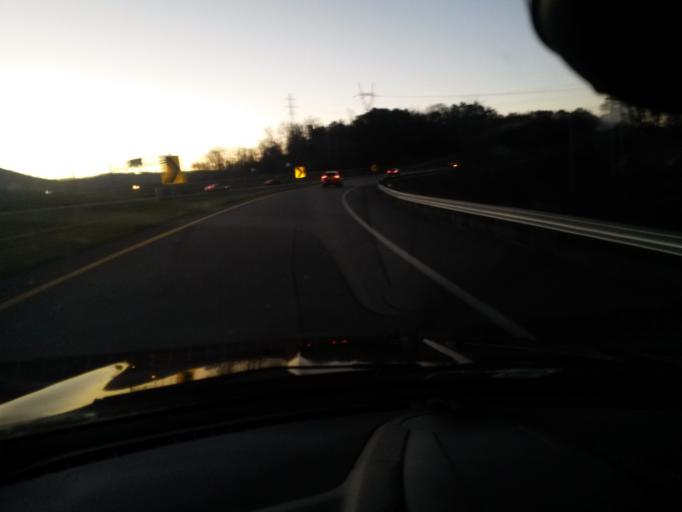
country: US
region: Virginia
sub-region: Botetourt County
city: Cloverdale
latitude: 37.3861
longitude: -79.9073
